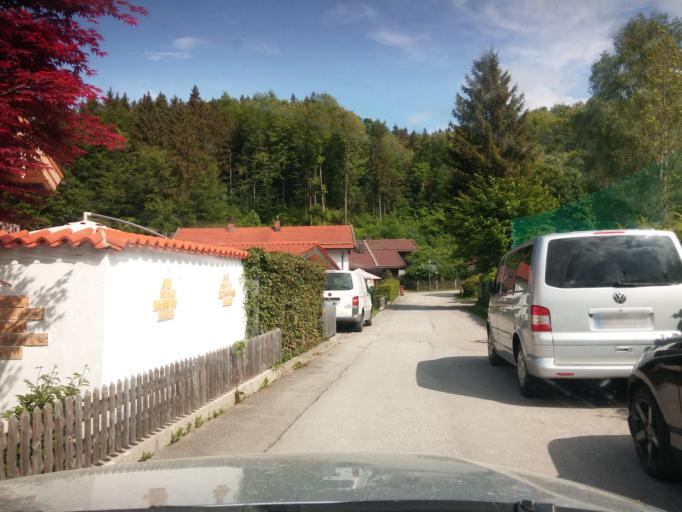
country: DE
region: Bavaria
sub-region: Upper Bavaria
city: Waakirchen
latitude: 47.7503
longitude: 11.6843
